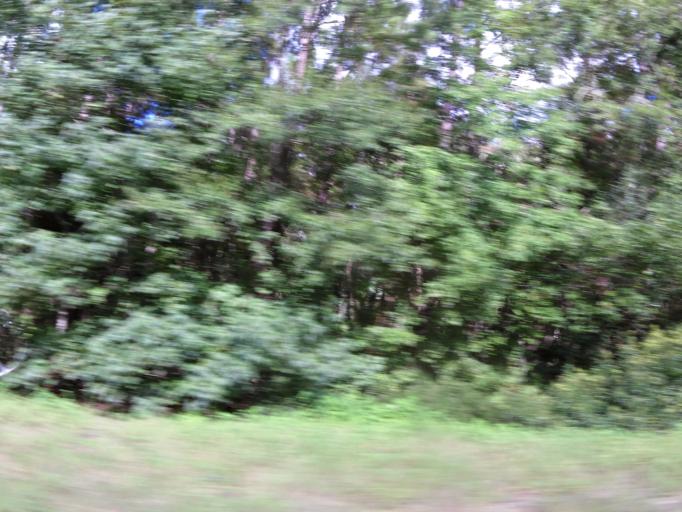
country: US
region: Georgia
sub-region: Camden County
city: Kingsland
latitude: 30.8256
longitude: -81.6953
